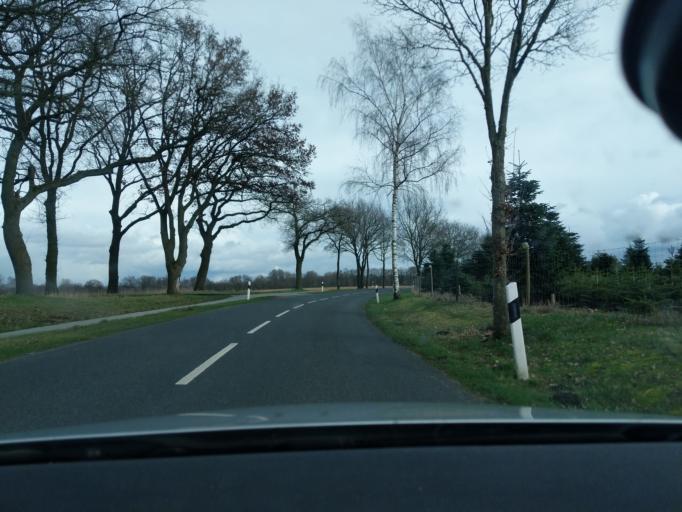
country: DE
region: Lower Saxony
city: Heinbockel
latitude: 53.5818
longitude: 9.3007
